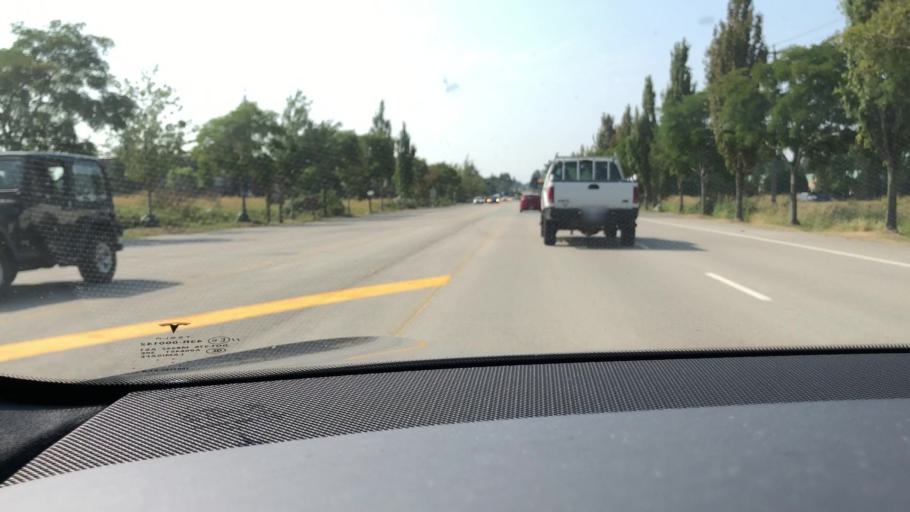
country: CA
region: British Columbia
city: Ladner
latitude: 49.0403
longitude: -123.0687
